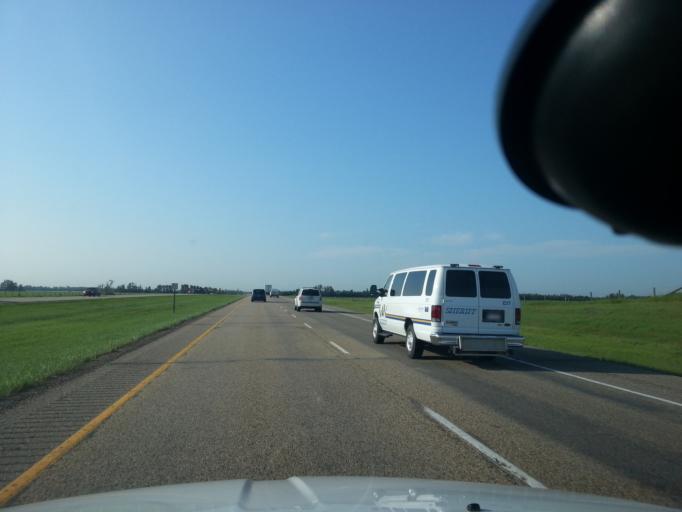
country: CA
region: Alberta
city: Leduc
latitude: 53.1564
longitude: -113.5984
